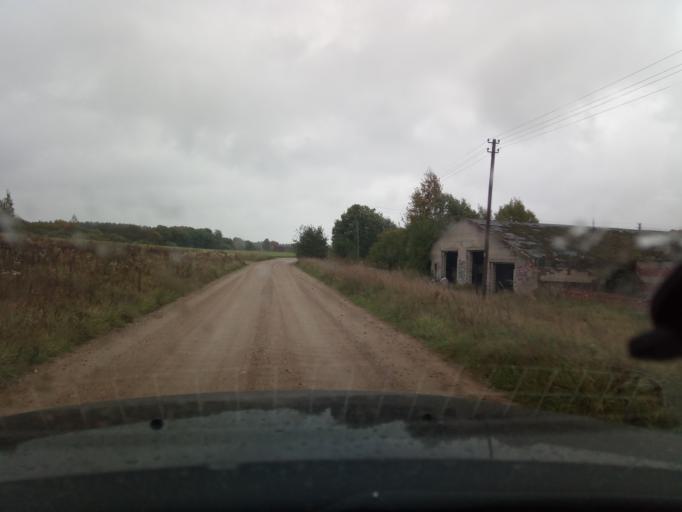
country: LT
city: Skaidiskes
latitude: 54.5947
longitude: 25.5756
